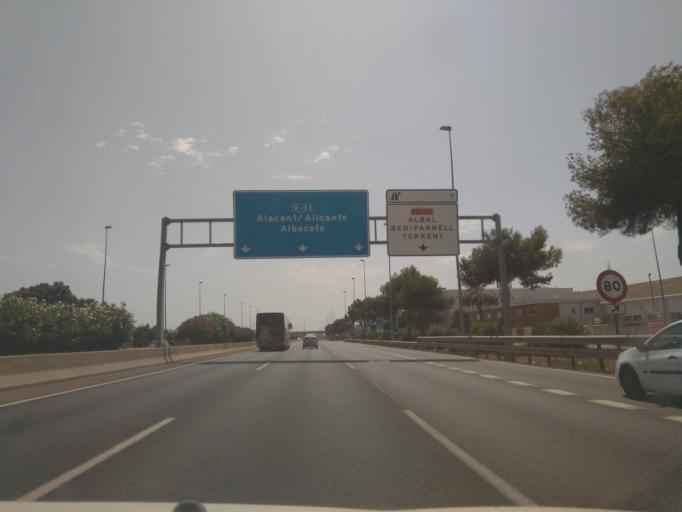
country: ES
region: Valencia
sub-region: Provincia de Valencia
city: Catarroja
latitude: 39.3911
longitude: -0.3934
